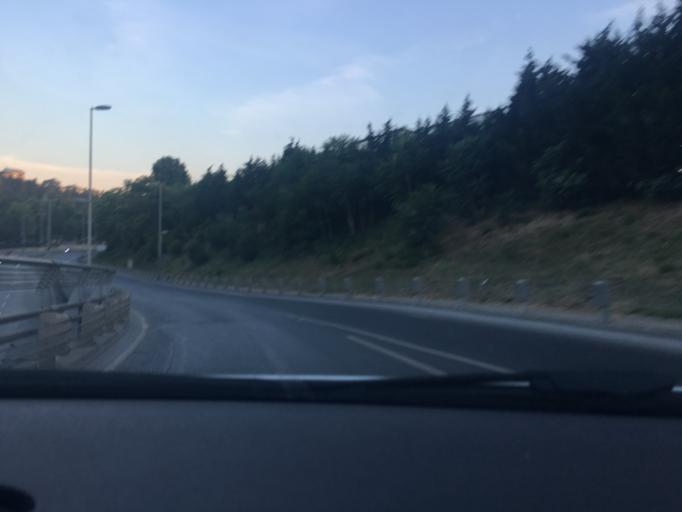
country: TR
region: Istanbul
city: Sisli
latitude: 41.0517
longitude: 28.9694
